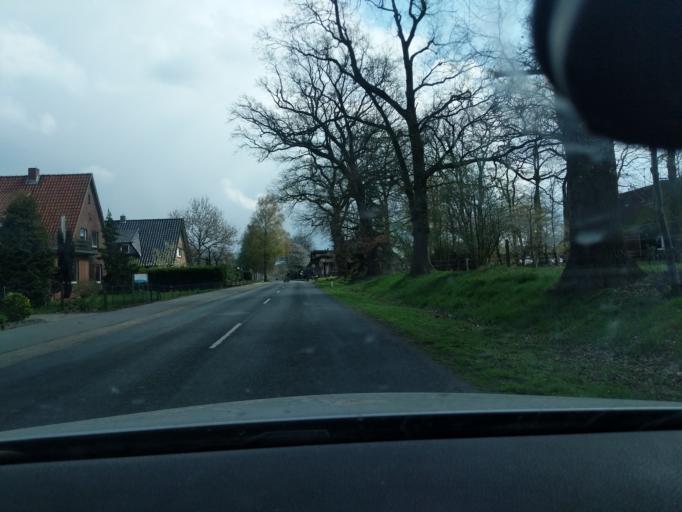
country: DE
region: Lower Saxony
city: Deinste
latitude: 53.5253
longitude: 9.4859
